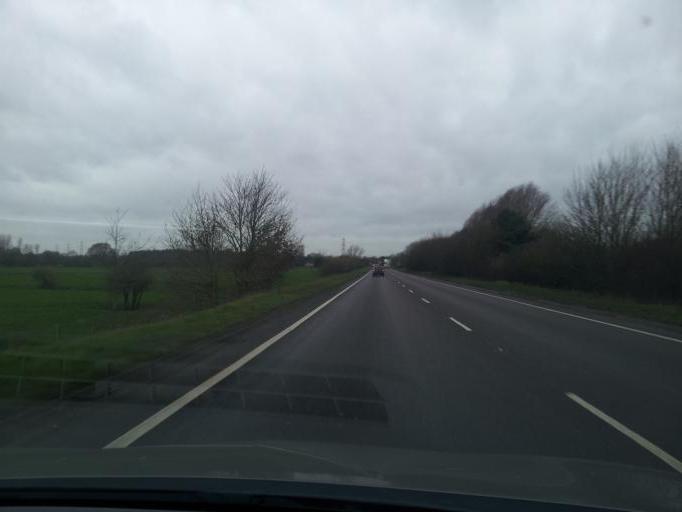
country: GB
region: England
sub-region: Norfolk
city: Diss
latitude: 52.3627
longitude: 1.1601
